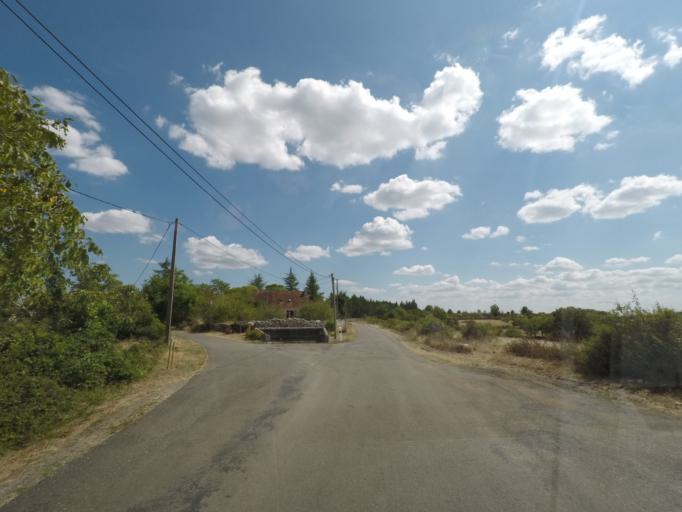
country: FR
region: Midi-Pyrenees
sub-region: Departement du Lot
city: Cajarc
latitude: 44.5431
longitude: 1.6693
